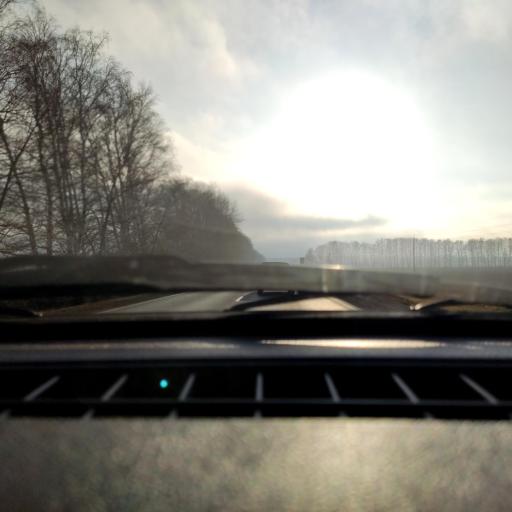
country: RU
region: Bashkortostan
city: Chishmy
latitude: 54.6561
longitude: 55.3909
